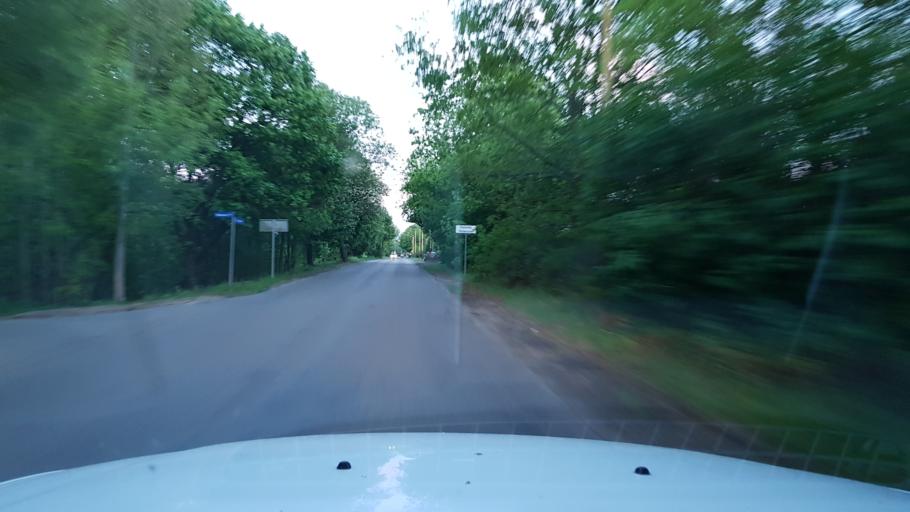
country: PL
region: West Pomeranian Voivodeship
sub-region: Powiat goleniowski
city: Goleniow
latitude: 53.5507
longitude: 14.8575
